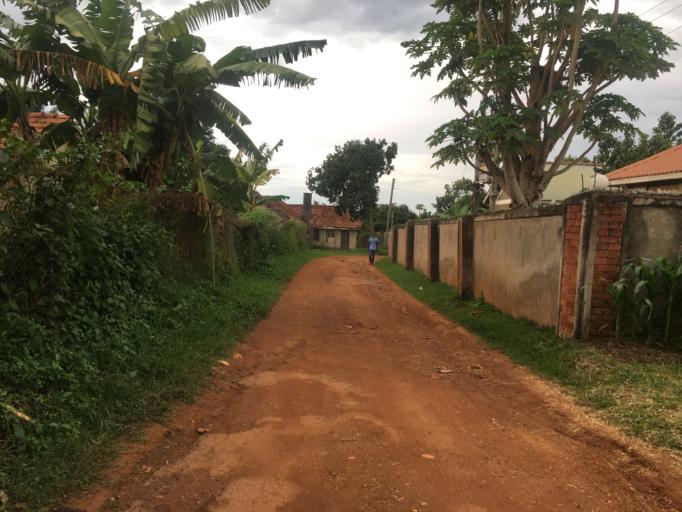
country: UG
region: Central Region
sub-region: Wakiso District
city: Entebbe
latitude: 0.0513
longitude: 32.4636
